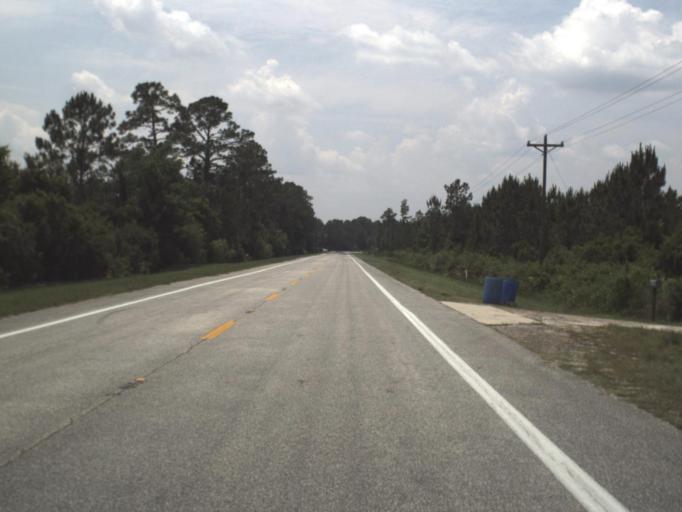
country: US
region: Florida
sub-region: Putnam County
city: Palatka
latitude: 29.5730
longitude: -81.7223
